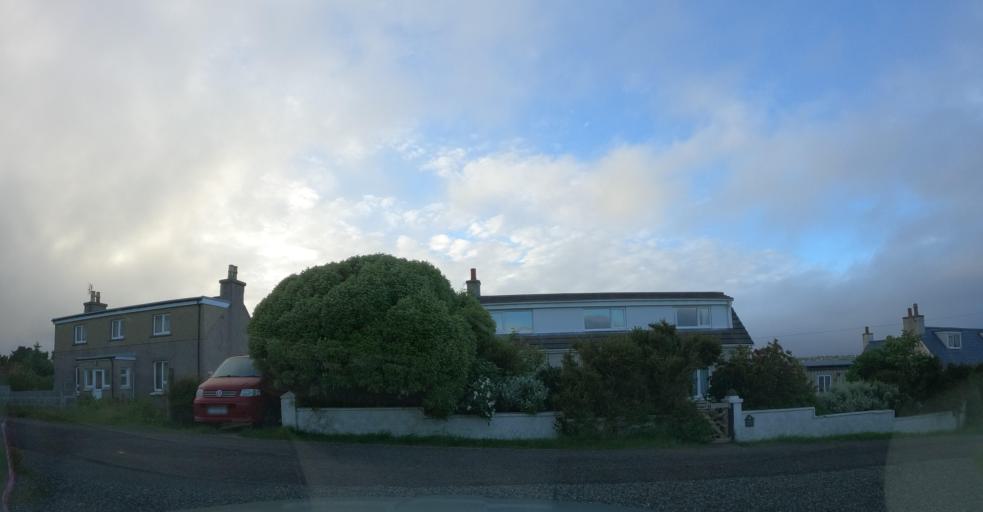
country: GB
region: Scotland
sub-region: Eilean Siar
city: Stornoway
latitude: 58.1943
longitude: -6.2173
